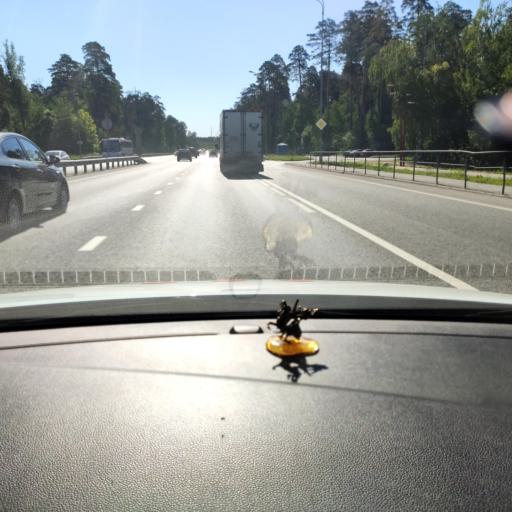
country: RU
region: Tatarstan
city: Staroye Arakchino
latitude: 55.8389
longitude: 48.9656
